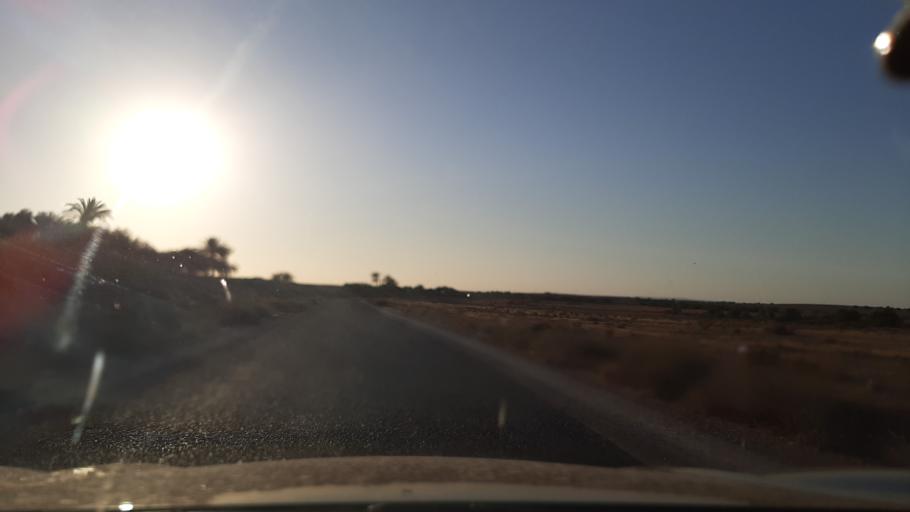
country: TN
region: Qabis
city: Matmata
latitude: 33.6236
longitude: 10.1375
